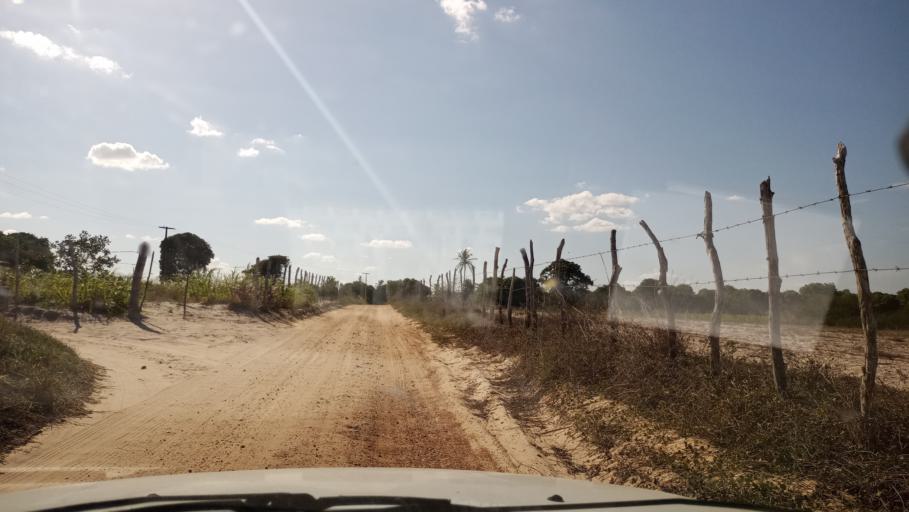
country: BR
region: Rio Grande do Norte
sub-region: Brejinho
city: Brejinho
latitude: -6.1761
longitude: -35.4613
